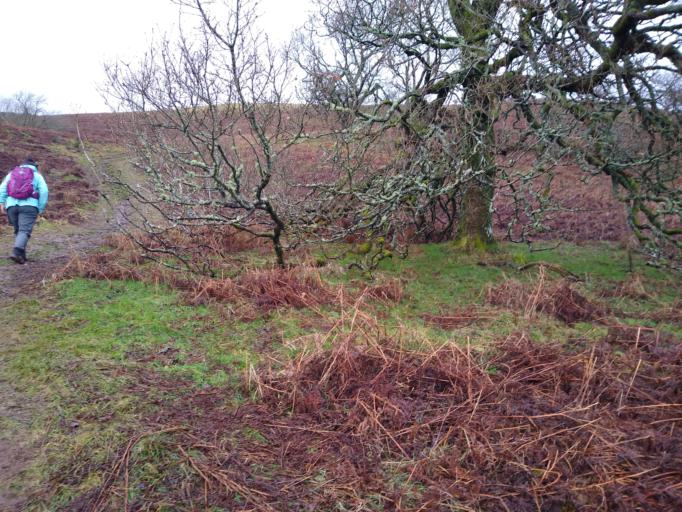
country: GB
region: England
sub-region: Cumbria
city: Penrith
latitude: 54.6131
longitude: -2.9266
